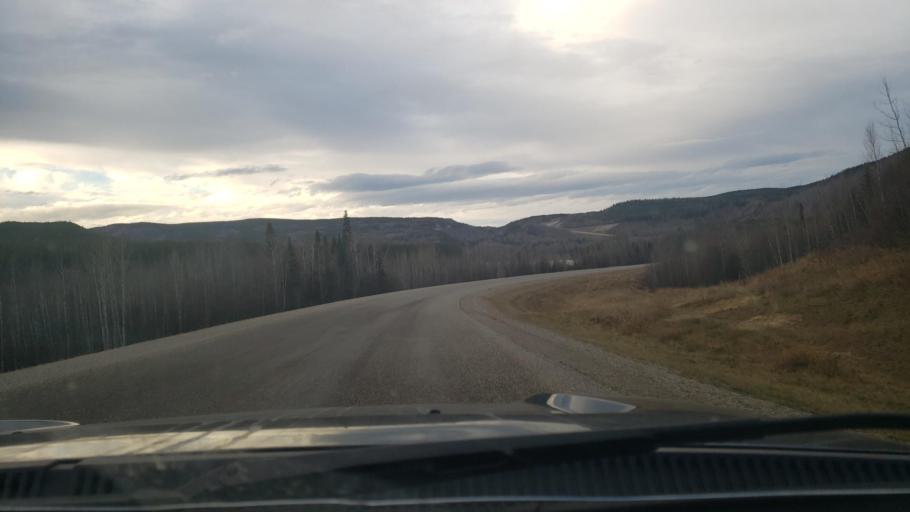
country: CA
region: Yukon
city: Watson Lake
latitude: 59.6989
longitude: -127.2245
